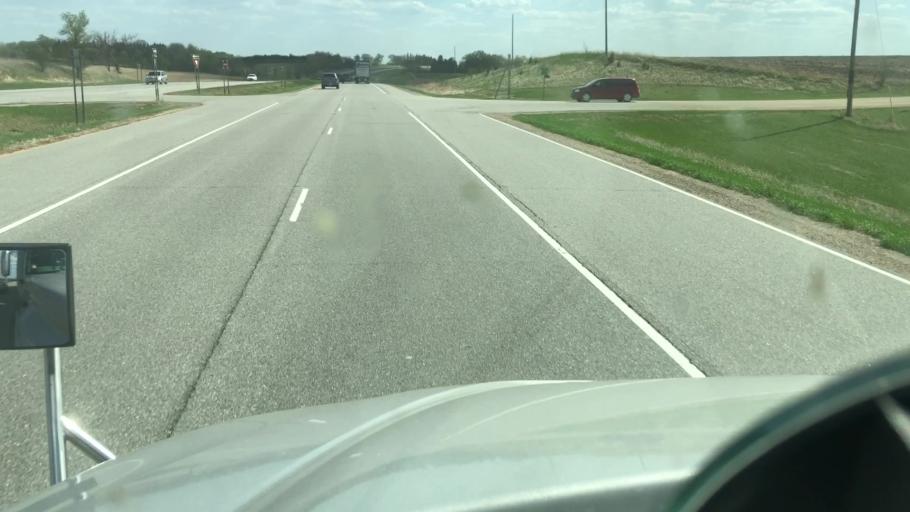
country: US
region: Minnesota
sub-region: Le Sueur County
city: Le Sueur
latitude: 44.5293
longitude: -93.8472
